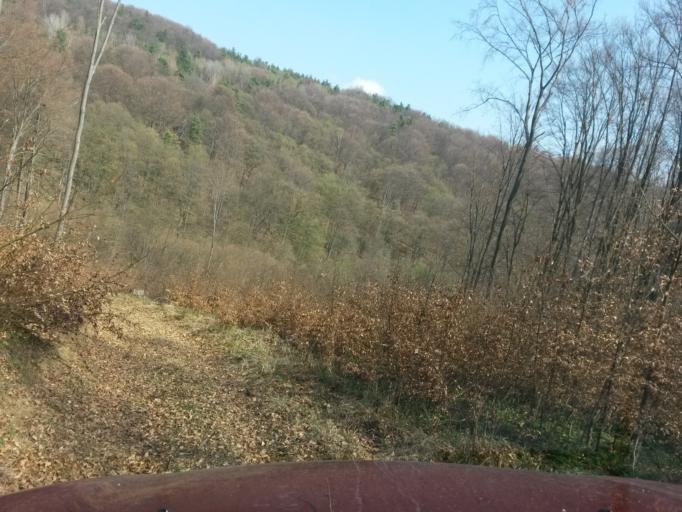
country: SK
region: Presovsky
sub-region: Okres Presov
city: Presov
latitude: 48.9366
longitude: 21.1461
